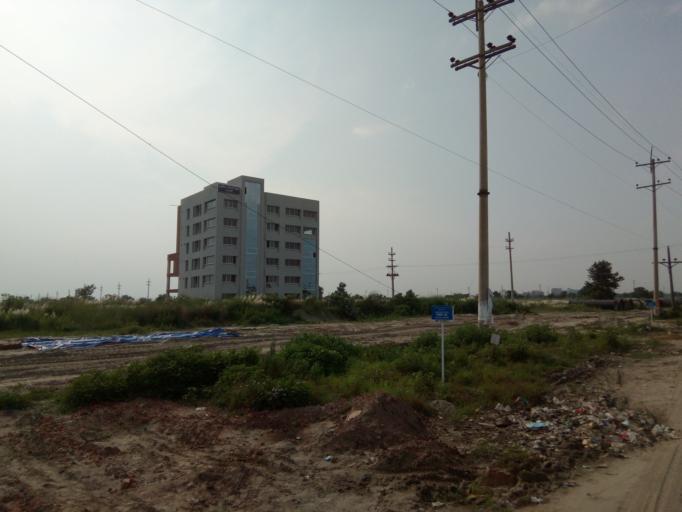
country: BD
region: Dhaka
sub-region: Dhaka
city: Dhaka
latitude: 23.6771
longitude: 90.4042
